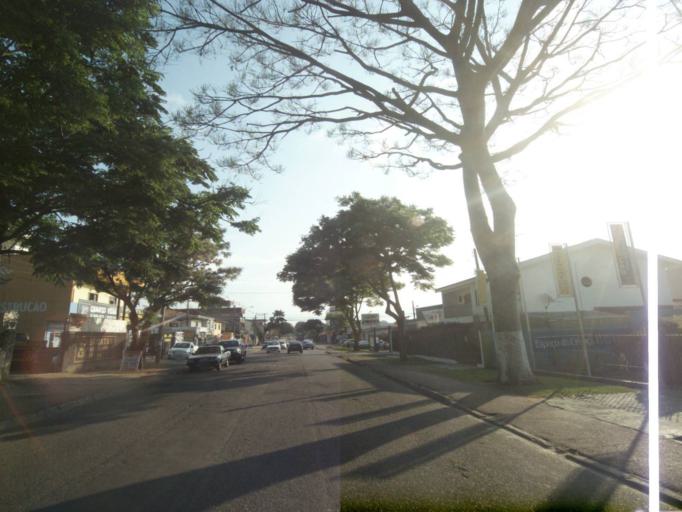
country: BR
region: Parana
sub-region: Curitiba
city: Curitiba
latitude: -25.4807
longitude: -49.3284
